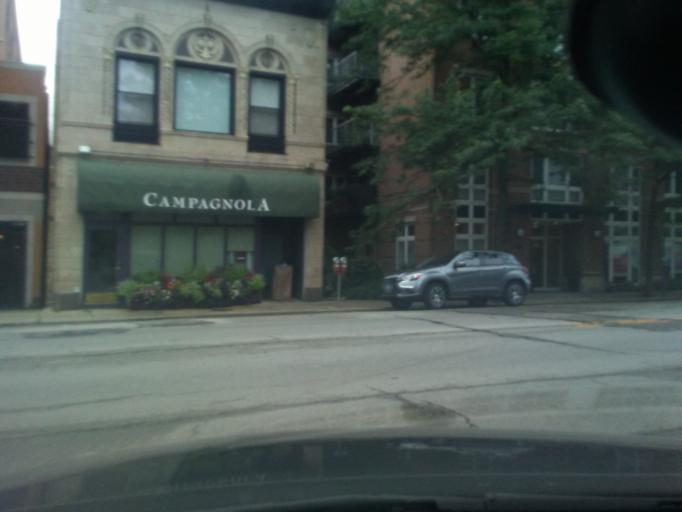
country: US
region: Illinois
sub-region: Cook County
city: Evanston
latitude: 42.0327
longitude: -87.6793
